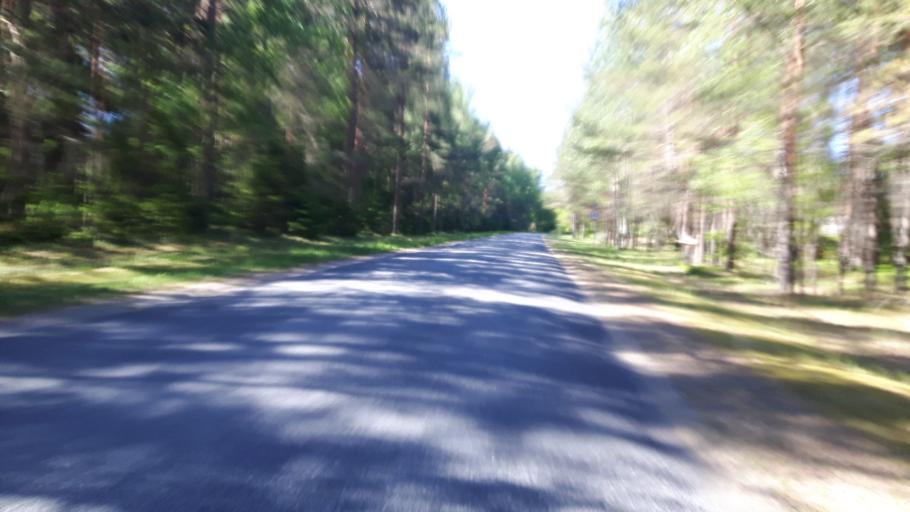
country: EE
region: Harju
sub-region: Loksa linn
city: Loksa
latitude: 59.5646
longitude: 25.6921
